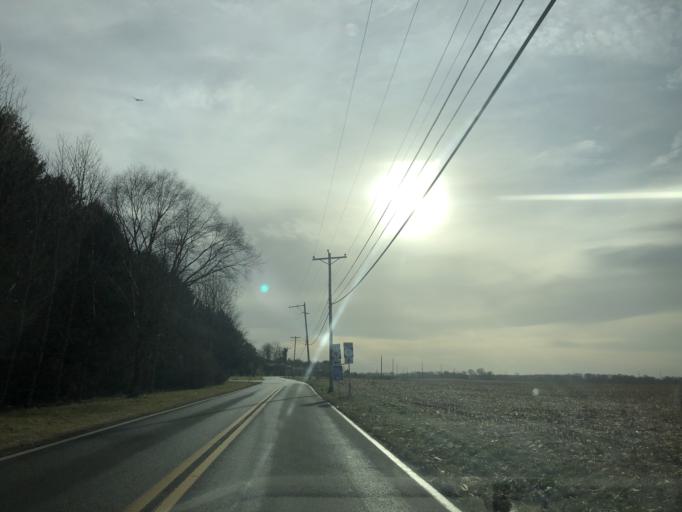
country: US
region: Delaware
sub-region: New Castle County
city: Townsend
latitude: 39.4390
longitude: -75.6424
